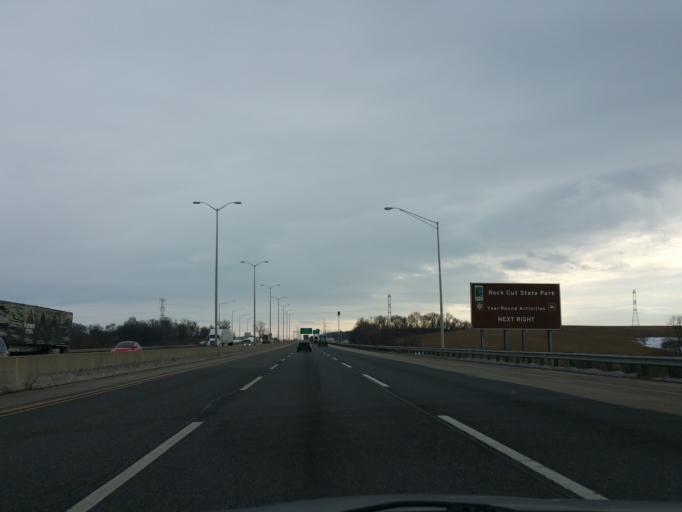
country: US
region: Illinois
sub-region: Winnebago County
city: Roscoe
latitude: 42.3830
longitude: -88.9721
